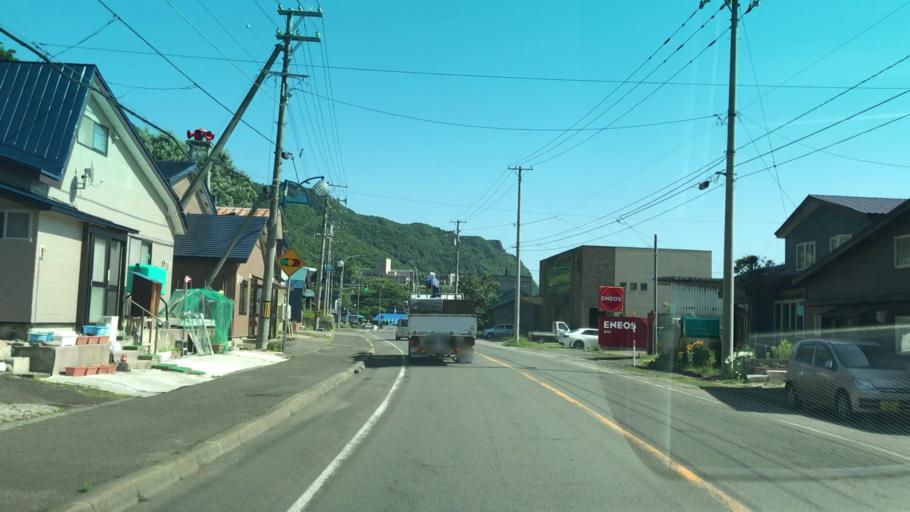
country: JP
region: Hokkaido
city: Iwanai
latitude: 43.1030
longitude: 140.4602
